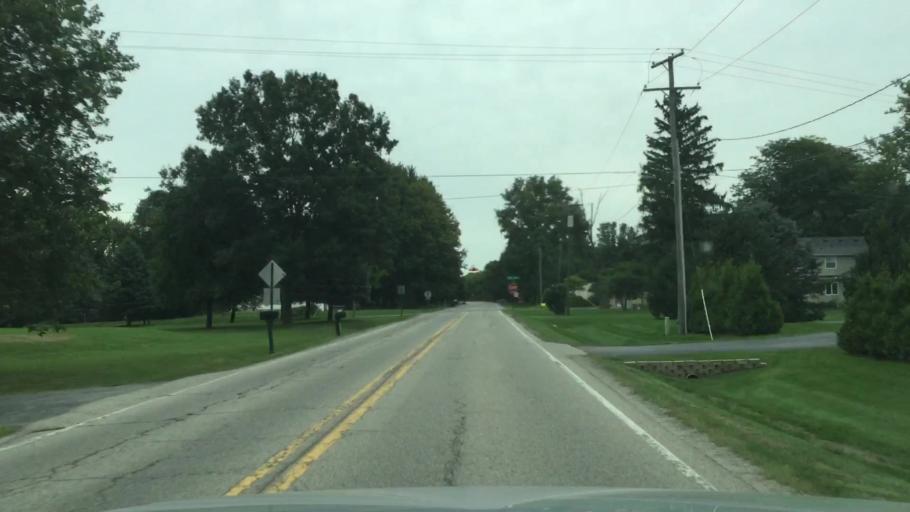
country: US
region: Michigan
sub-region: Washtenaw County
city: Milan
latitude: 42.1109
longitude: -83.7246
